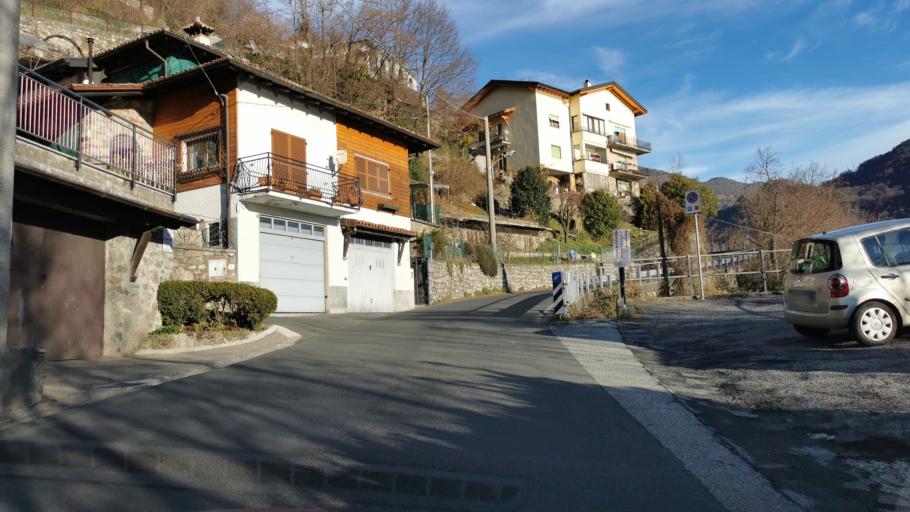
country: IT
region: Lombardy
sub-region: Provincia di Como
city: Menaggio
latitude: 46.0326
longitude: 9.2315
